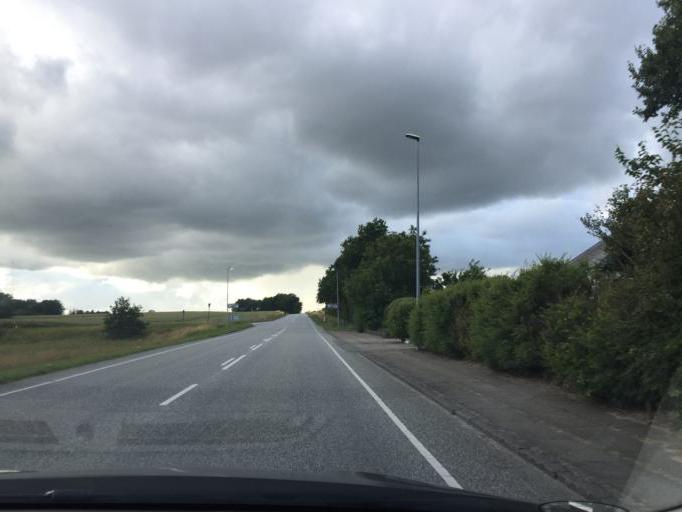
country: DK
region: South Denmark
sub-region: Haderslev Kommune
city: Vojens
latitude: 55.3229
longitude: 9.2599
